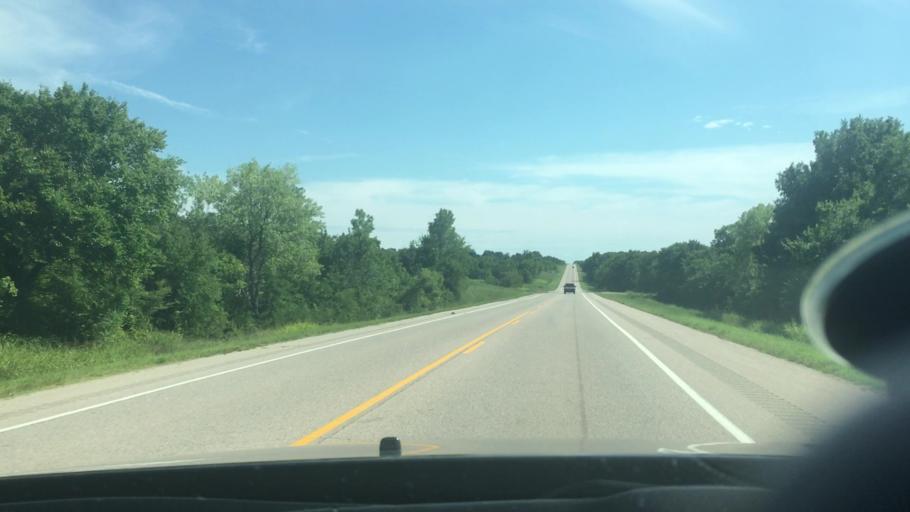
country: US
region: Oklahoma
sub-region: Seminole County
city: Konawa
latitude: 35.0122
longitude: -96.6786
